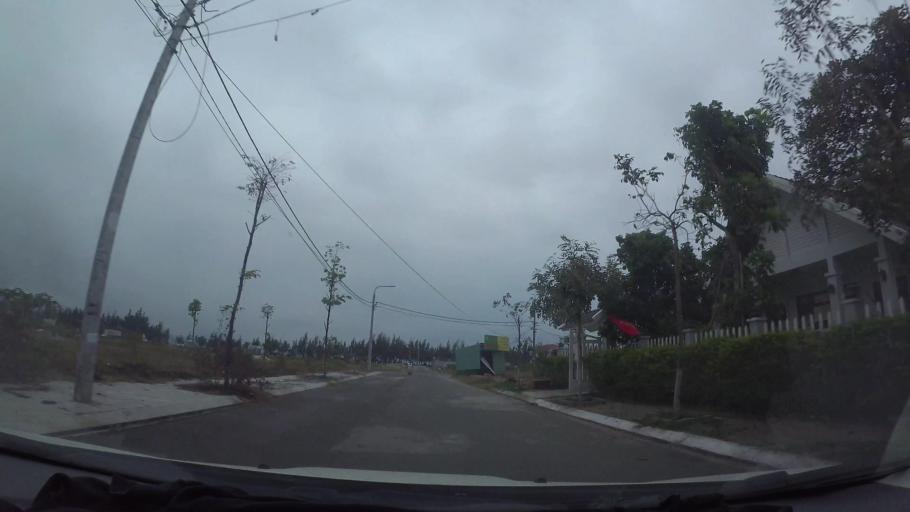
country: VN
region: Da Nang
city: Lien Chieu
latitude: 16.0884
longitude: 108.1514
